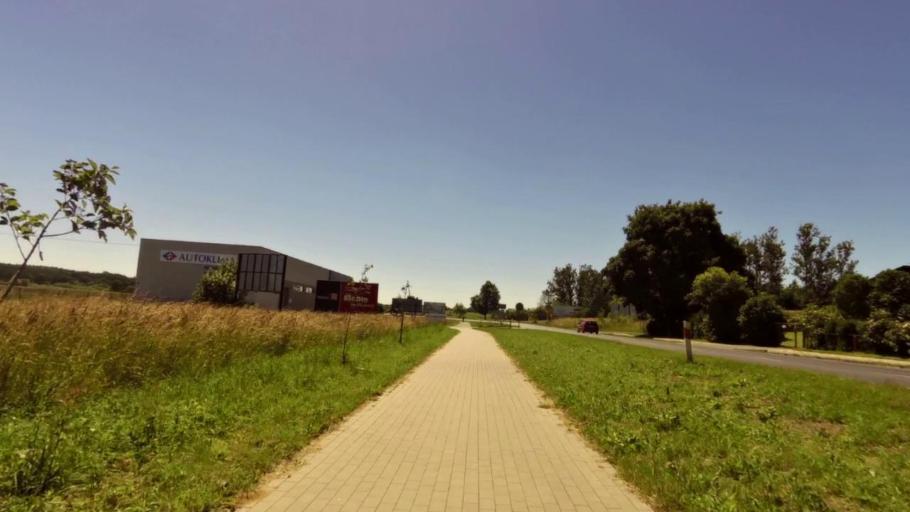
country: PL
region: West Pomeranian Voivodeship
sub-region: Powiat kolobrzeski
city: Kolobrzeg
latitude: 54.1382
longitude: 15.5590
